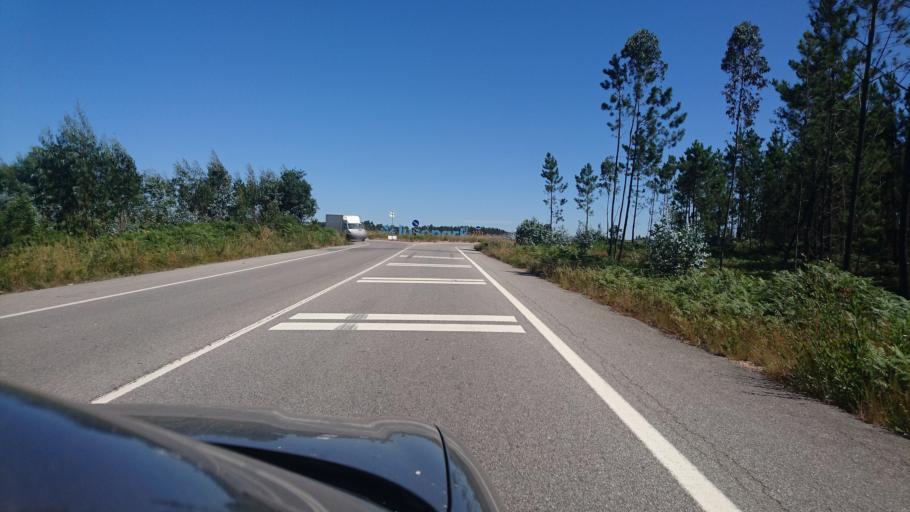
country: PT
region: Aveiro
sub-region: Santa Maria da Feira
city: Rio Meao
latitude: 40.9375
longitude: -8.5816
